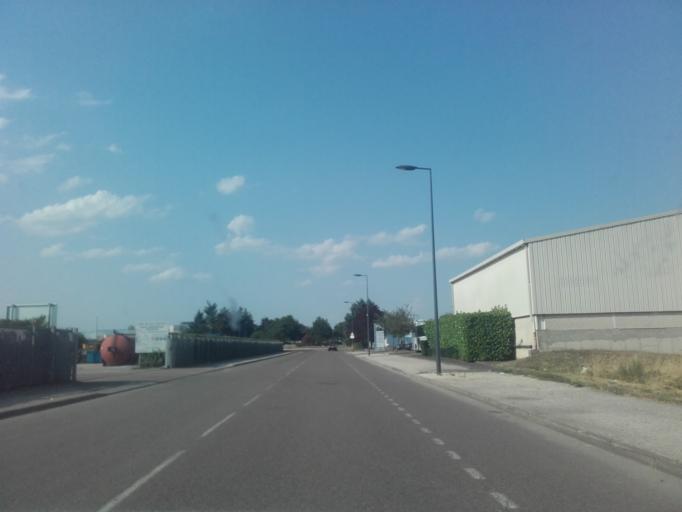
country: FR
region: Bourgogne
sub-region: Departement de la Cote-d'Or
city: Beaune
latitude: 47.0227
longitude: 4.8657
